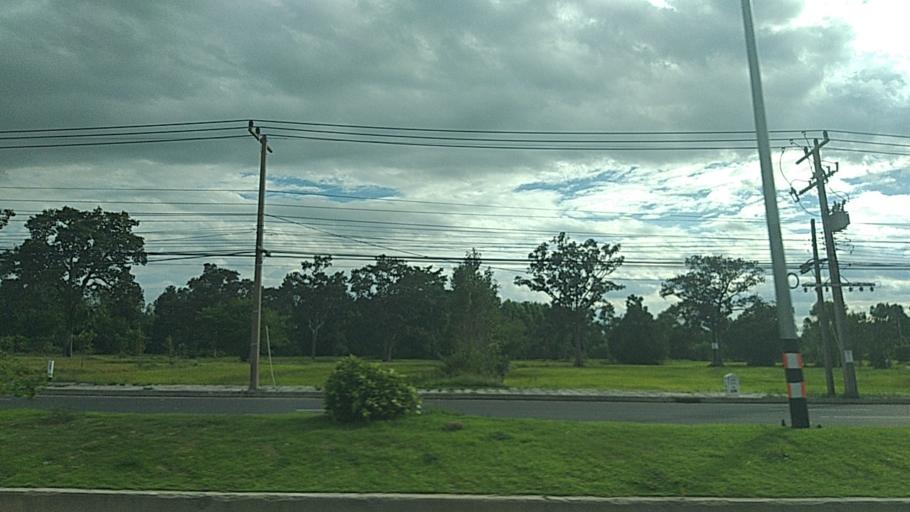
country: TH
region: Surin
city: Prasat
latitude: 14.6160
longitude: 103.4159
